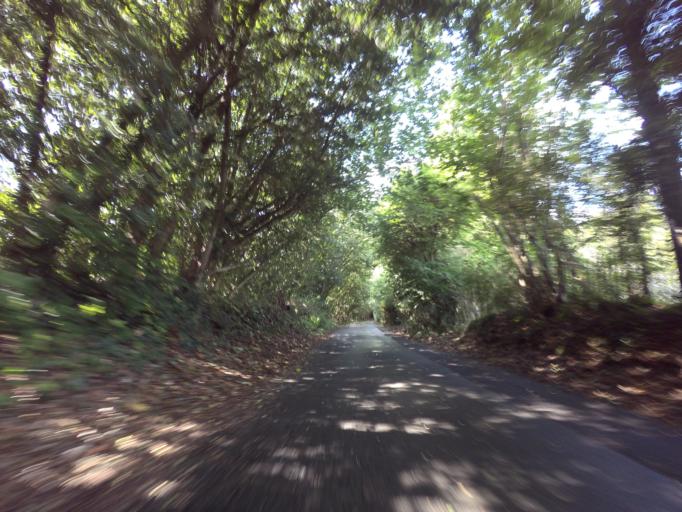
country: GB
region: England
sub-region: Kent
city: Borough Green
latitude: 51.2723
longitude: 0.2795
